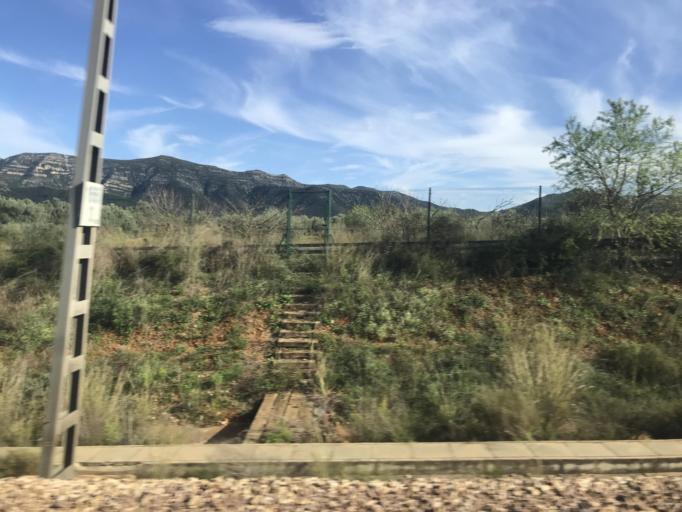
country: ES
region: Catalonia
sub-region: Provincia de Tarragona
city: Ulldecona
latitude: 40.6223
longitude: 0.4780
